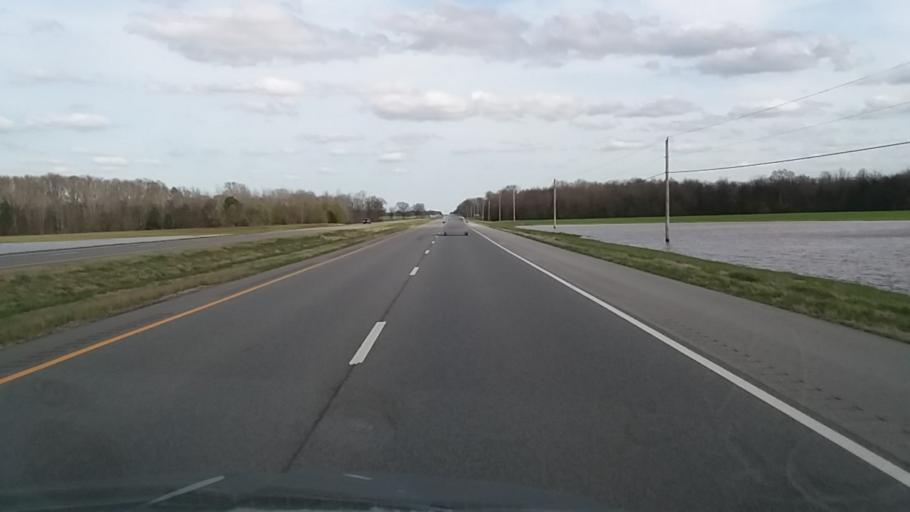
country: US
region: Alabama
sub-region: Colbert County
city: Muscle Shoals
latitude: 34.6843
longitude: -87.5519
